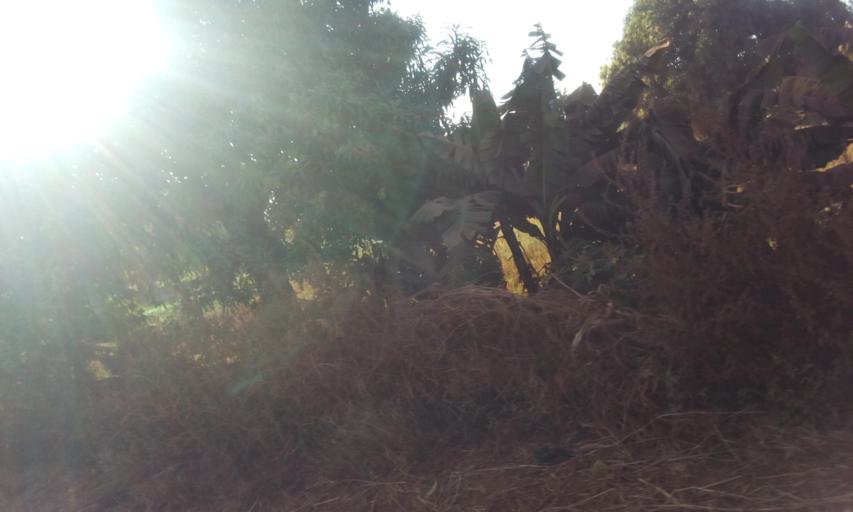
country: ML
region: Bamako
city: Bamako
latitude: 12.6459
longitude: -7.9038
